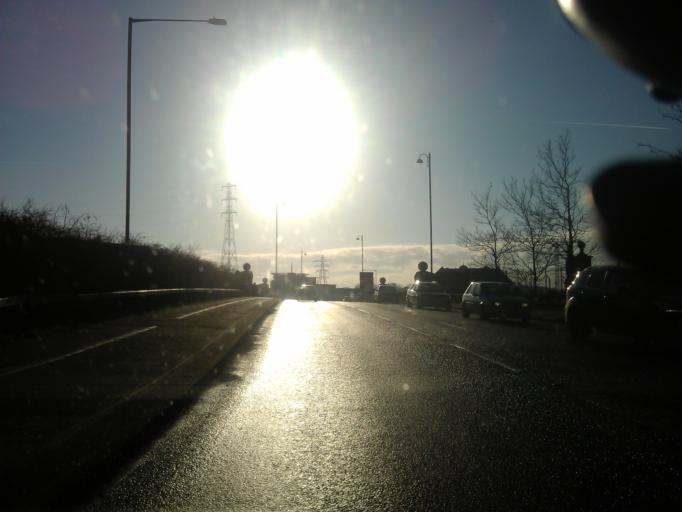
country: GB
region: England
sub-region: Essex
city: Rowhedge
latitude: 51.8830
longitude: 0.9327
